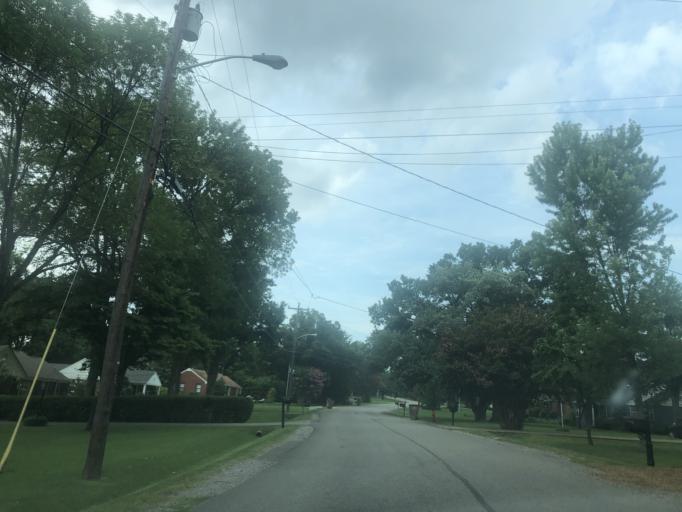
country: US
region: Tennessee
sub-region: Davidson County
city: Lakewood
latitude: 36.1576
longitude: -86.6847
